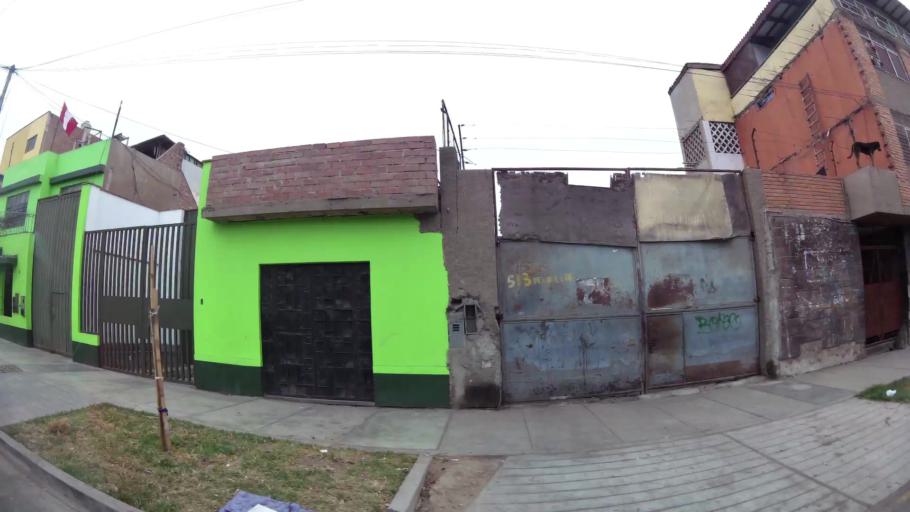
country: PE
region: Lima
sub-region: Lima
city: Surco
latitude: -12.1515
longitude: -77.0178
